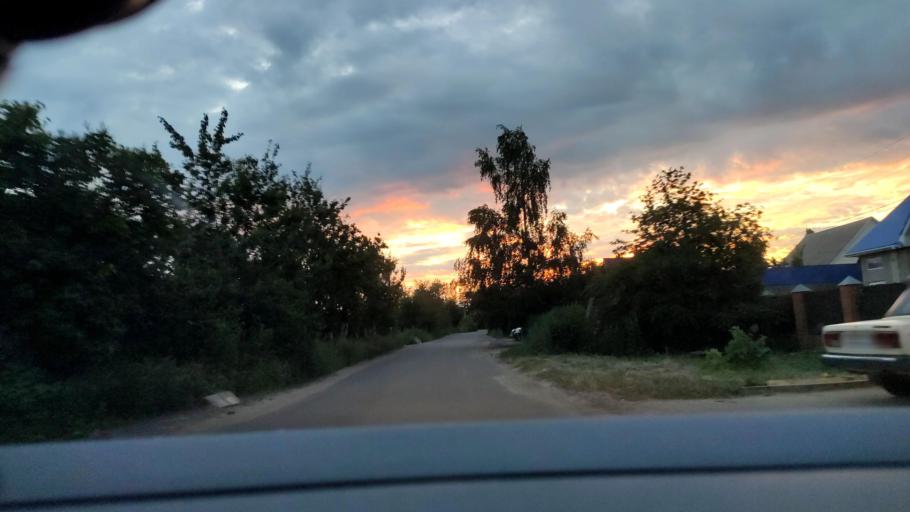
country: RU
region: Voronezj
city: Semiluki
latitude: 51.7044
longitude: 39.0225
